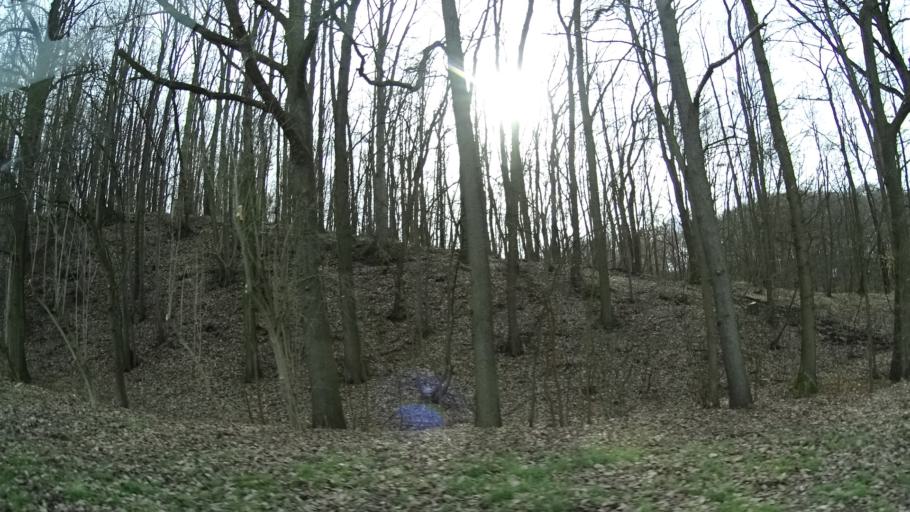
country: DE
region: Thuringia
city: Sulza
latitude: 50.8695
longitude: 11.6224
